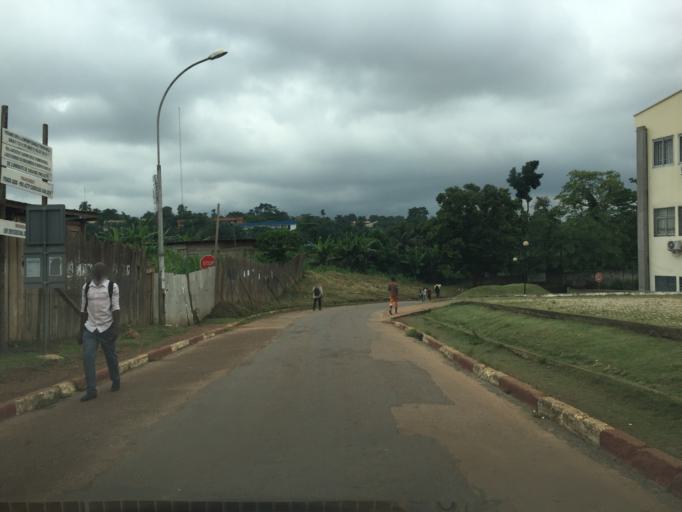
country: CM
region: Centre
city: Yaounde
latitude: 3.8615
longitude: 11.4973
